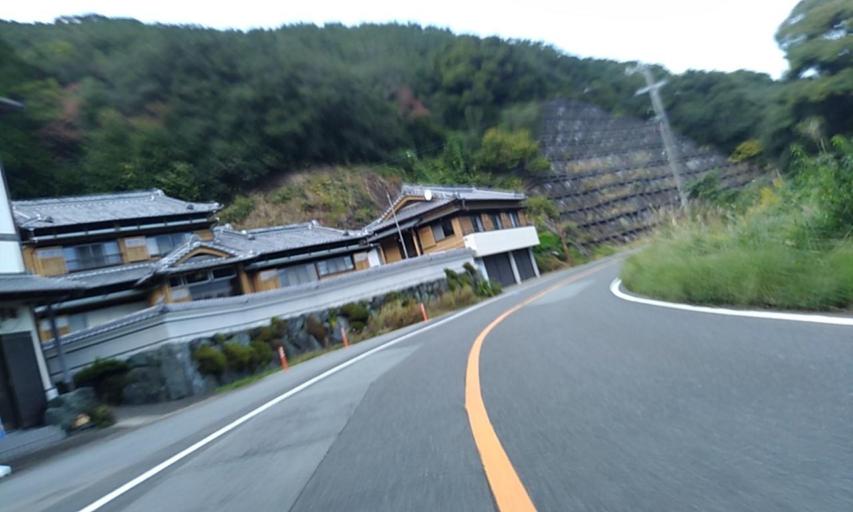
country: JP
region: Mie
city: Ise
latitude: 34.3193
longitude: 136.6492
